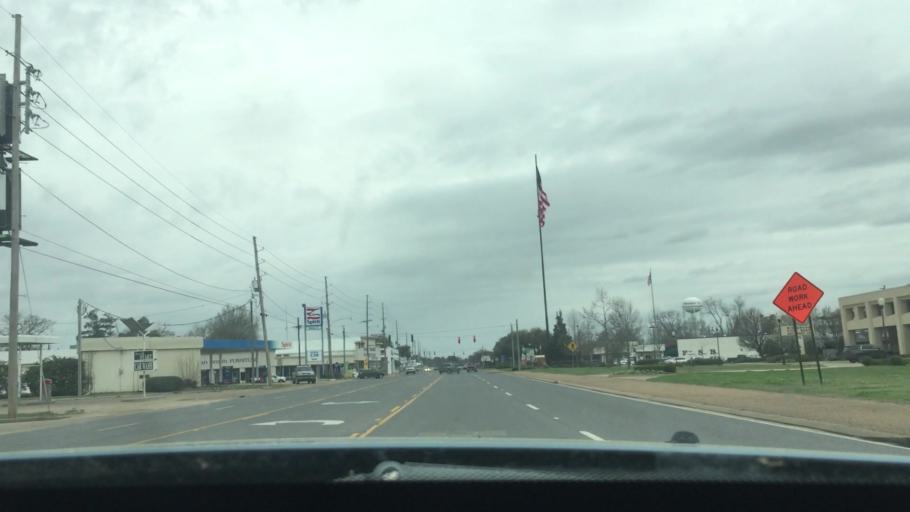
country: US
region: Louisiana
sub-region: Franklin Parish
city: Winnsboro
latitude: 32.1625
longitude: -91.7193
